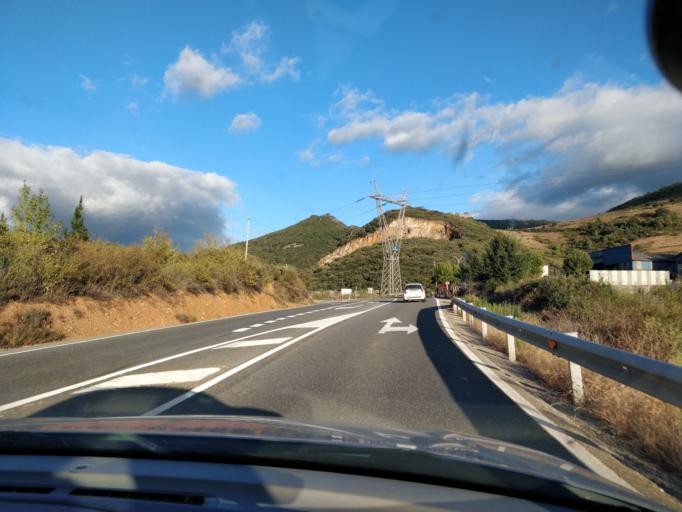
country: ES
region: Castille and Leon
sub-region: Provincia de Leon
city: Borrenes
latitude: 42.4916
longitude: -6.7036
